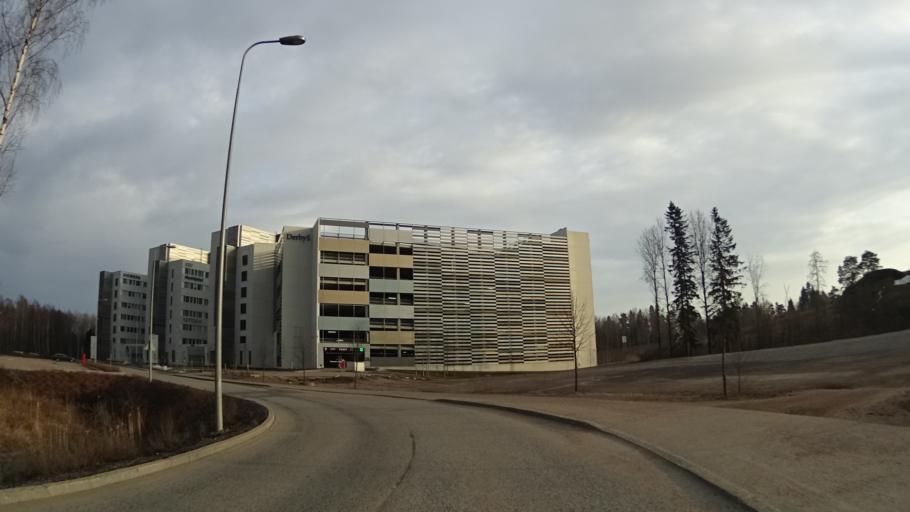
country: FI
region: Uusimaa
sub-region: Helsinki
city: Teekkarikylae
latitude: 60.2100
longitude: 24.8336
